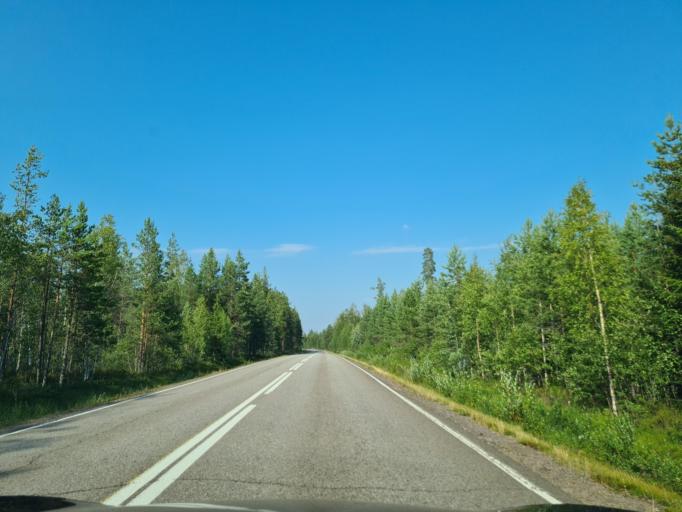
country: FI
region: Satakunta
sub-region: Pohjois-Satakunta
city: Karvia
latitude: 62.3167
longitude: 22.6612
